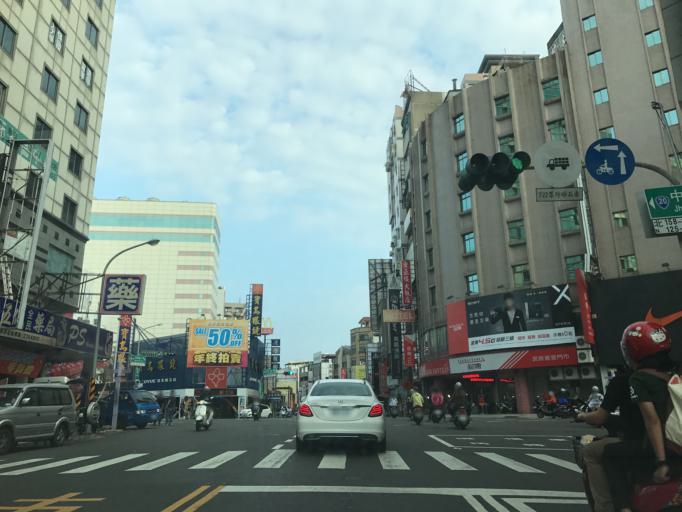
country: TW
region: Taiwan
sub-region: Tainan
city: Tainan
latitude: 22.9949
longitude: 120.2081
